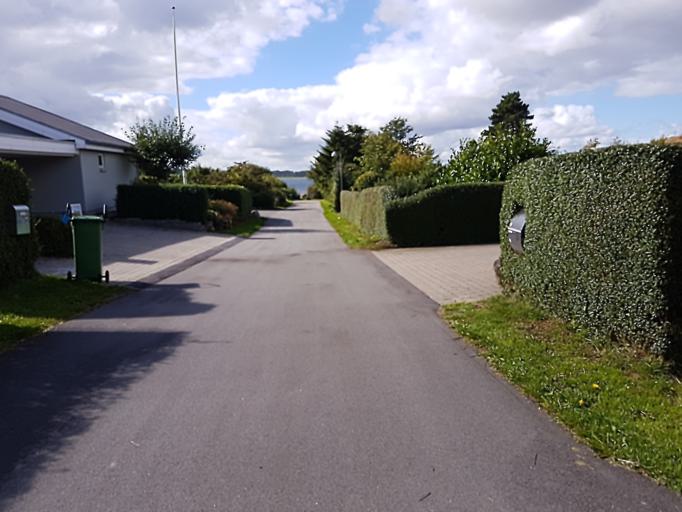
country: DK
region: Zealand
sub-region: Roskilde Kommune
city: Jyllinge
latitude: 55.7695
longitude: 12.0914
